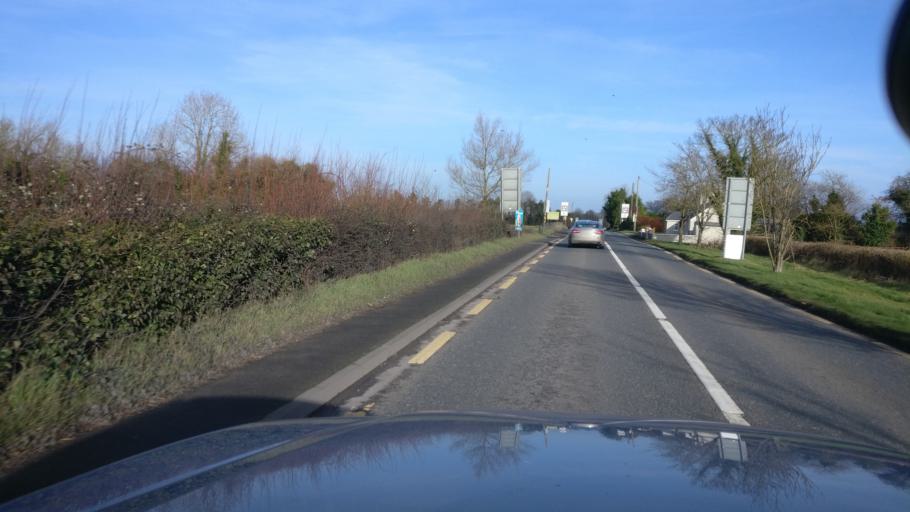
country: IE
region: Leinster
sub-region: Laois
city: Mountmellick
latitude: 53.1032
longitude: -7.3363
